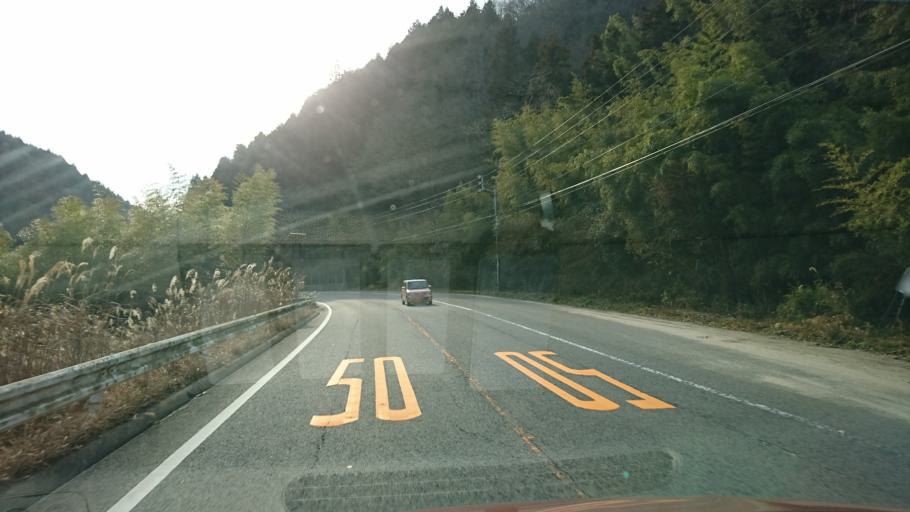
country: JP
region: Ehime
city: Hojo
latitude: 33.9296
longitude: 132.8953
